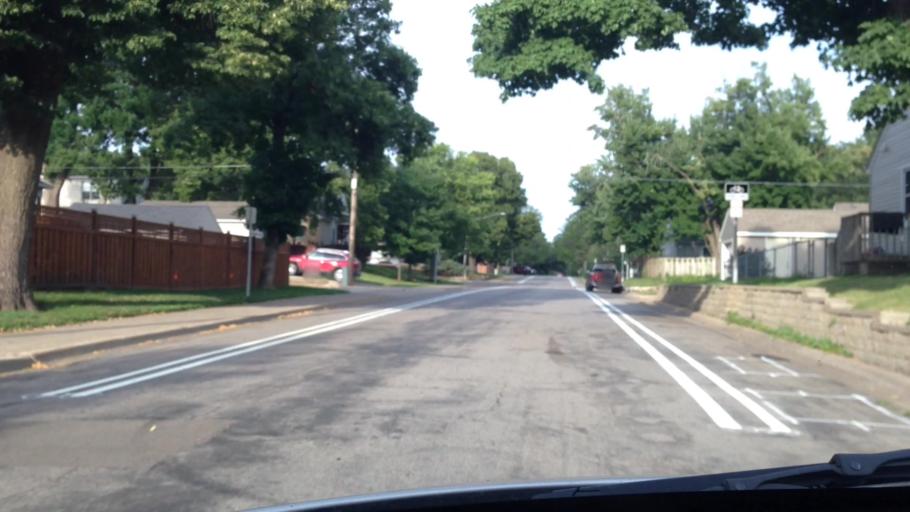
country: US
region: Minnesota
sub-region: Hennepin County
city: Saint Louis Park
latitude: 44.9531
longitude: -93.3683
